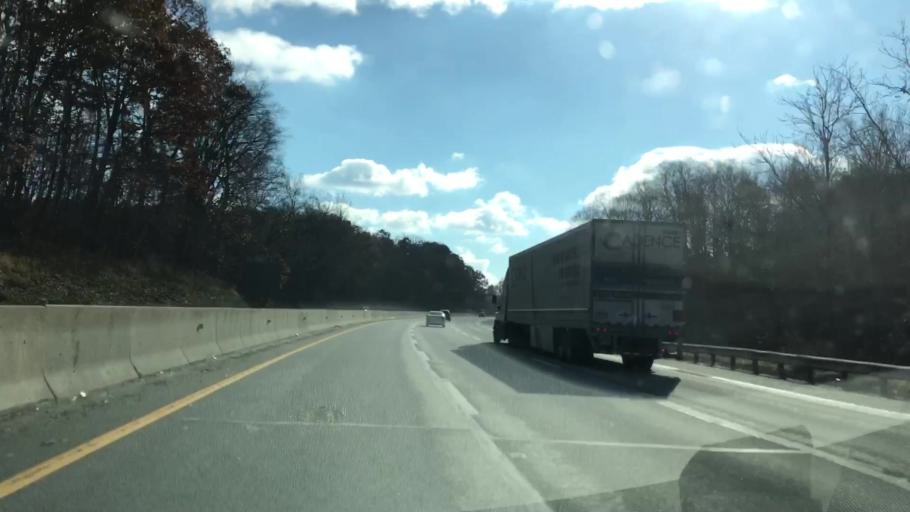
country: US
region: Pennsylvania
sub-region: Beaver County
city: West Mayfield
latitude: 40.8051
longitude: -80.3019
